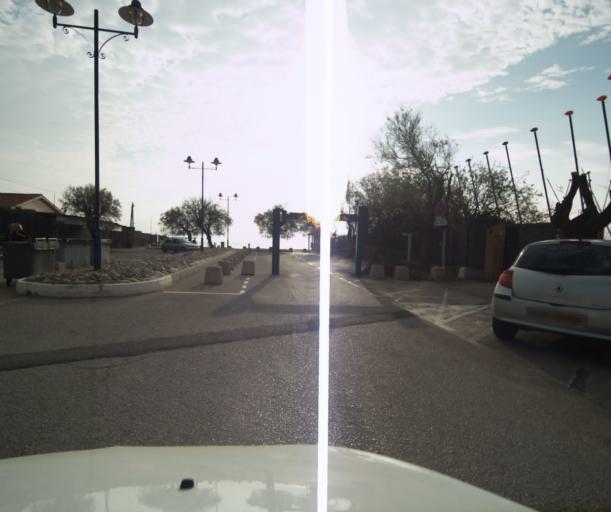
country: FR
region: Provence-Alpes-Cote d'Azur
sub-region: Departement du Var
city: Hyeres
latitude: 43.0478
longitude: 6.1489
